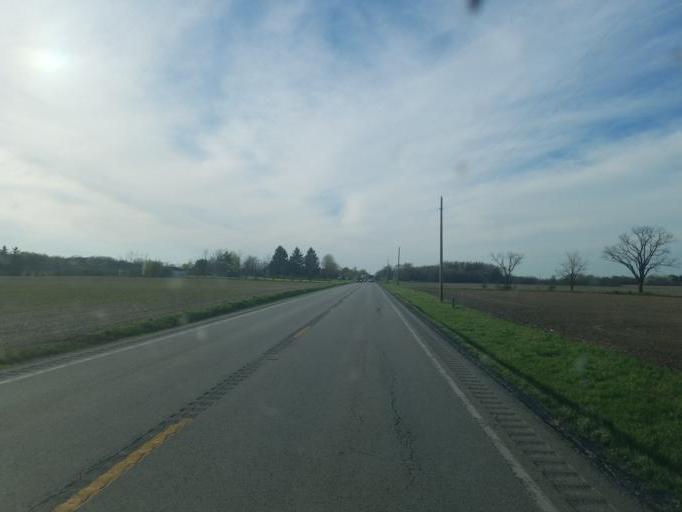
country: US
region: Ohio
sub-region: Huron County
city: Greenwich
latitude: 41.1191
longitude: -82.5099
